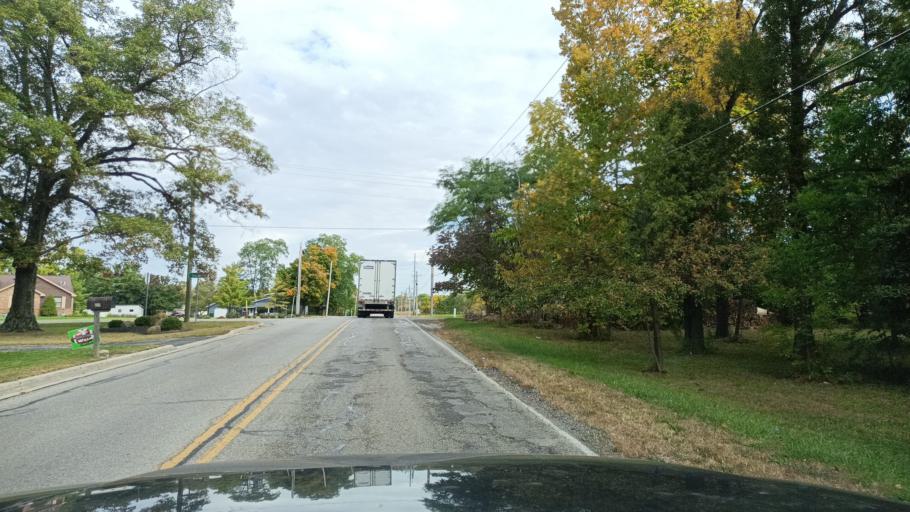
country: US
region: Indiana
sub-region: Delaware County
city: Yorktown
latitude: 40.1997
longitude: -85.4615
